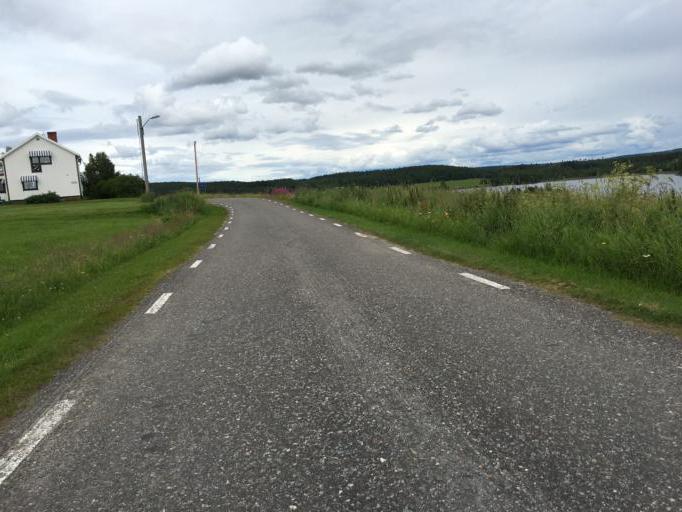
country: SE
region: Norrbotten
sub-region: Overkalix Kommun
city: OEverkalix
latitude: 66.1085
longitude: 22.7867
